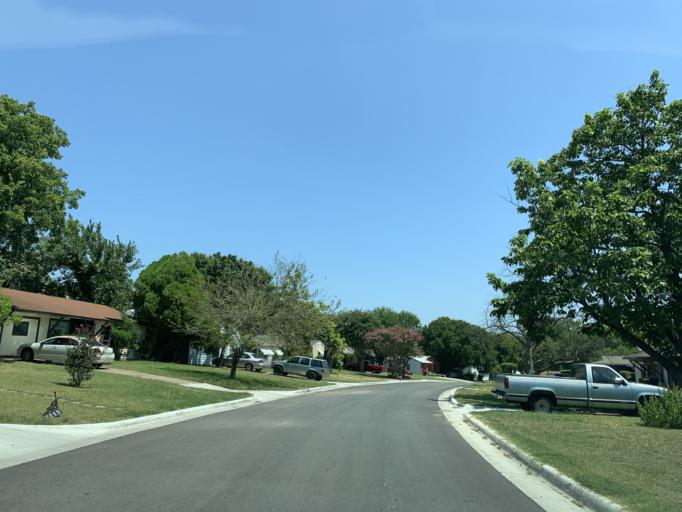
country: US
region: Texas
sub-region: Dallas County
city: Hutchins
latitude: 32.6773
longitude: -96.7606
